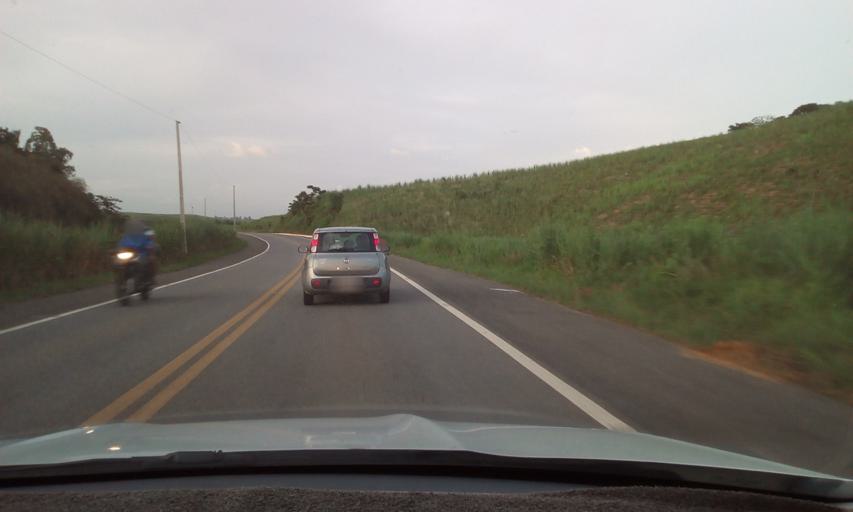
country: BR
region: Pernambuco
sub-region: Vicencia
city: Vicencia
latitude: -7.6387
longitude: -35.2538
